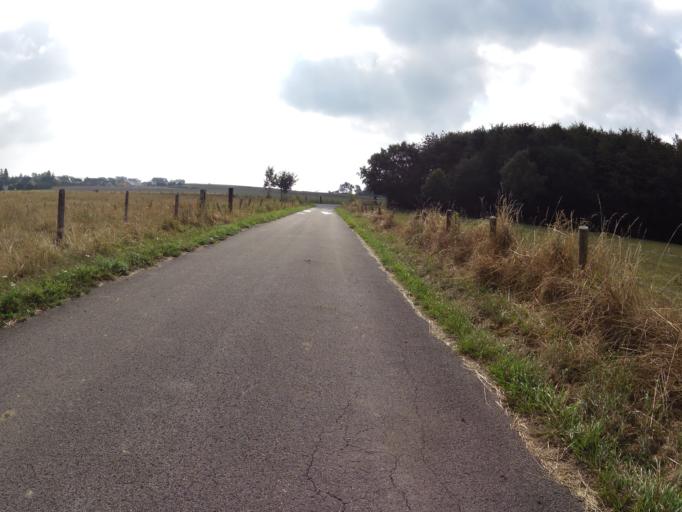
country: DE
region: North Rhine-Westphalia
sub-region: Regierungsbezirk Koln
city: Blankenheim
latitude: 50.4371
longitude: 6.6144
